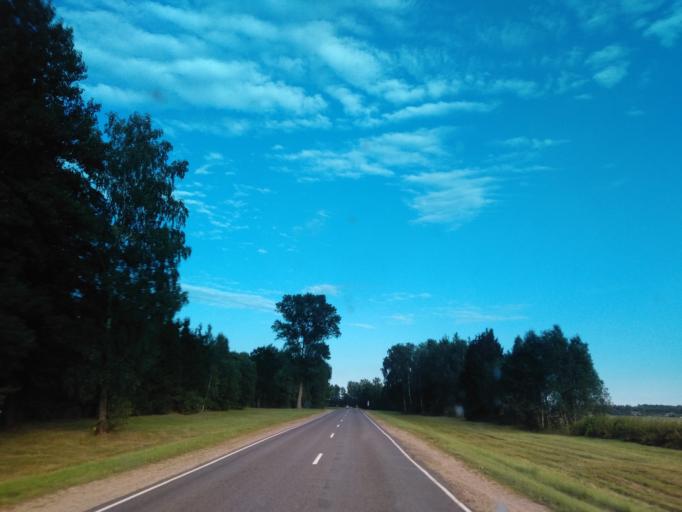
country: BY
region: Minsk
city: Uzda
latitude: 53.4424
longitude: 27.2855
